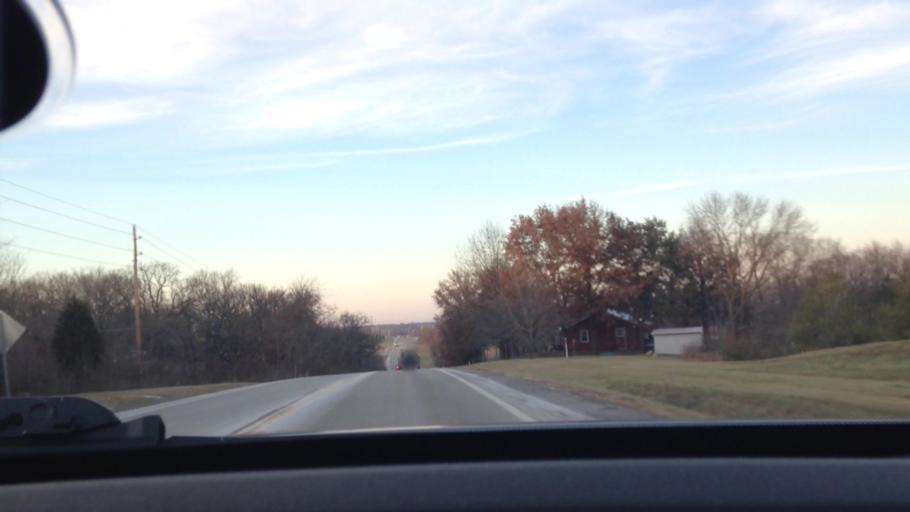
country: US
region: Missouri
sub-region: Clay County
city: Liberty
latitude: 39.2724
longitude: -94.4626
